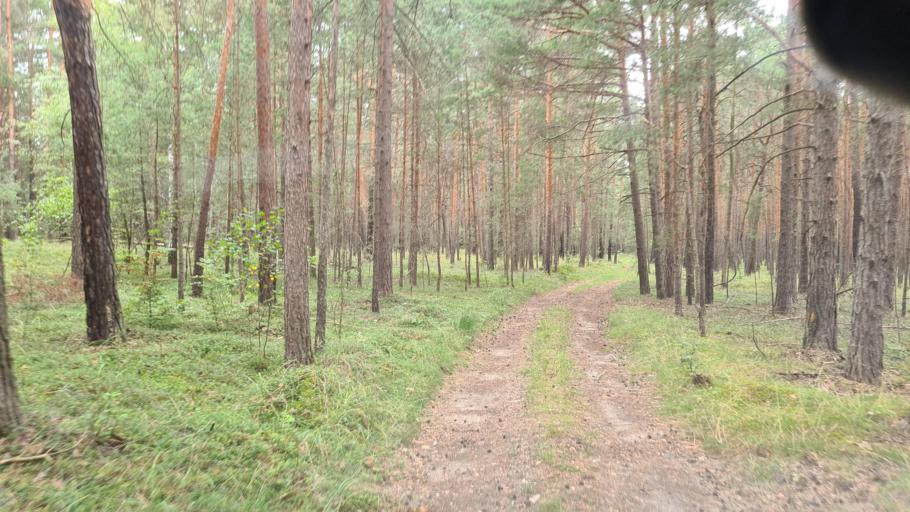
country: DE
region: Brandenburg
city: Sallgast
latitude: 51.5853
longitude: 13.8917
